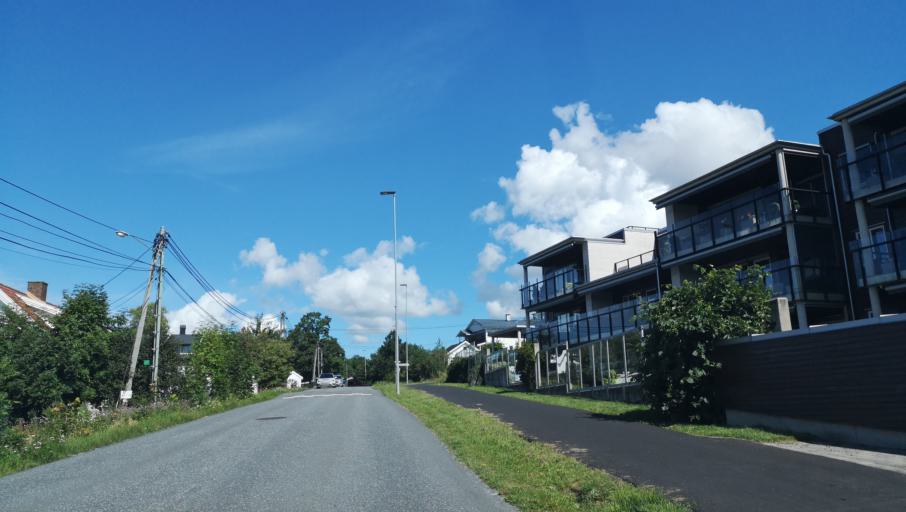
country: NO
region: Akershus
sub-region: Frogn
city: Drobak
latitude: 59.6548
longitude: 10.6411
